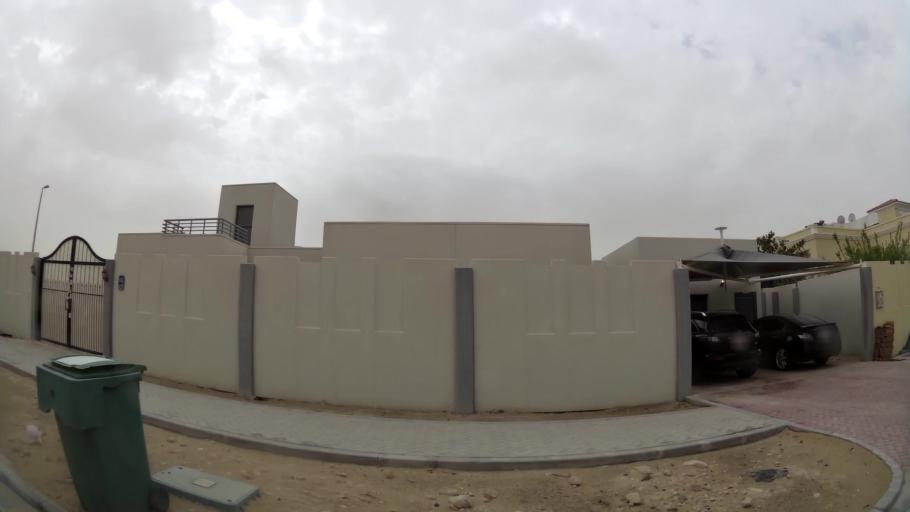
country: AE
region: Abu Dhabi
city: Abu Dhabi
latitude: 24.4565
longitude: 54.7317
